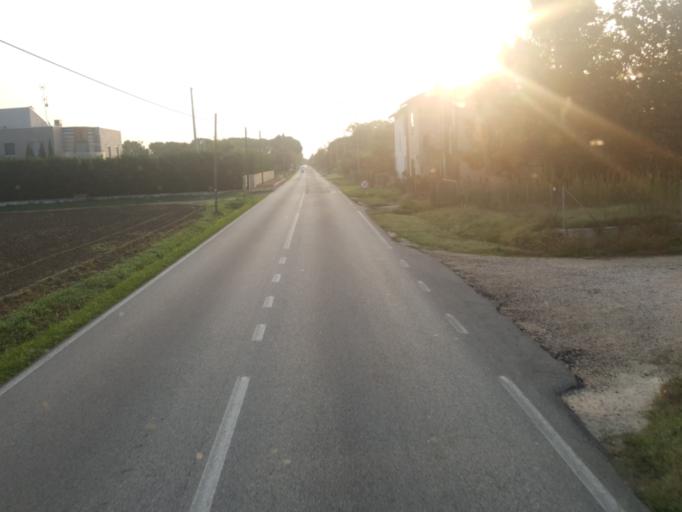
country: IT
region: Emilia-Romagna
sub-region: Provincia di Ravenna
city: Lavezzola
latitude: 44.5577
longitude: 11.8667
